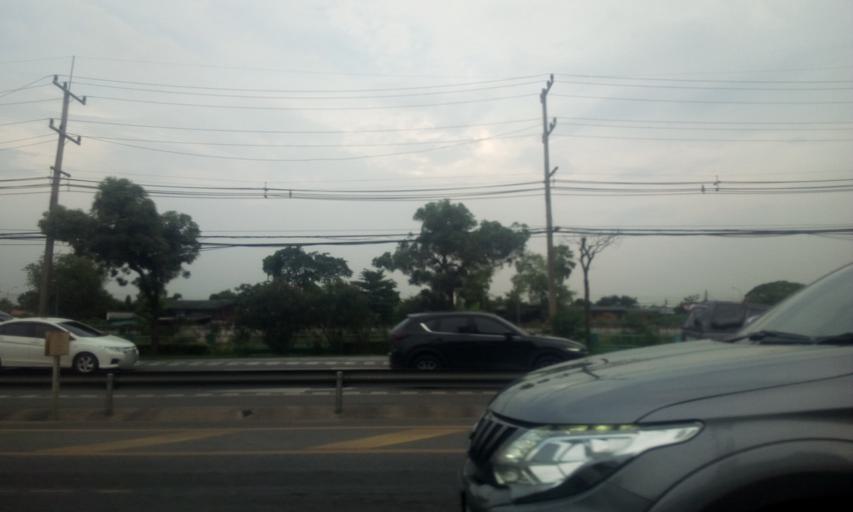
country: TH
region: Pathum Thani
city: Thanyaburi
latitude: 13.9996
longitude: 100.6842
